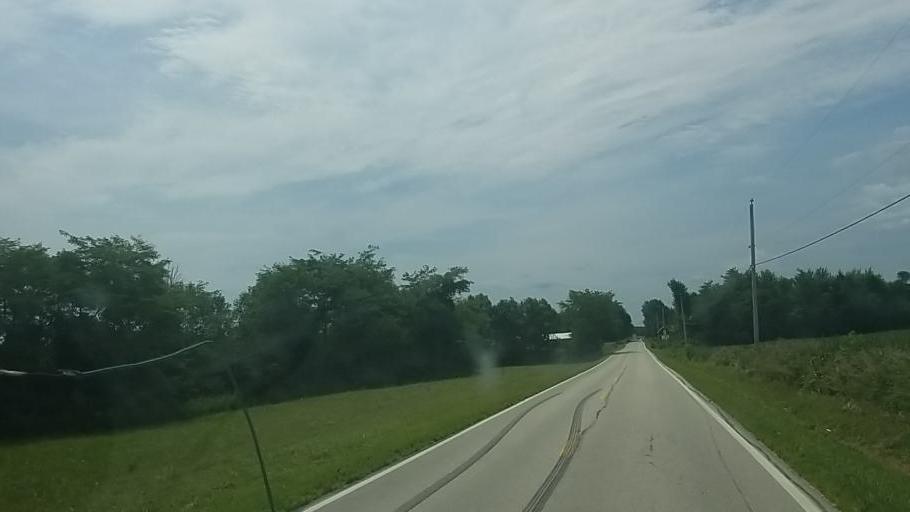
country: US
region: Ohio
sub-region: Delaware County
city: Sunbury
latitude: 40.2009
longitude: -82.8261
